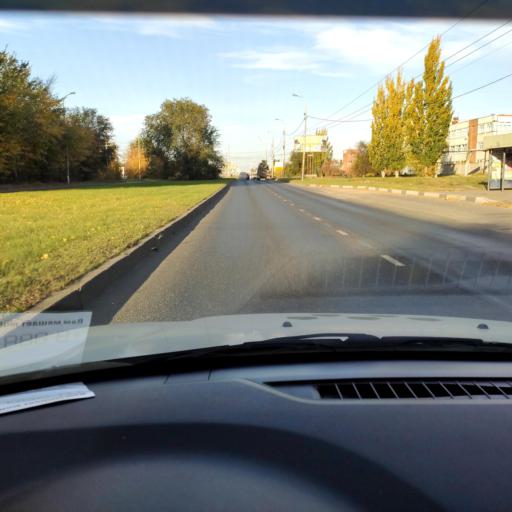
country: RU
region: Samara
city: Tol'yatti
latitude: 53.5605
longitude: 49.2981
